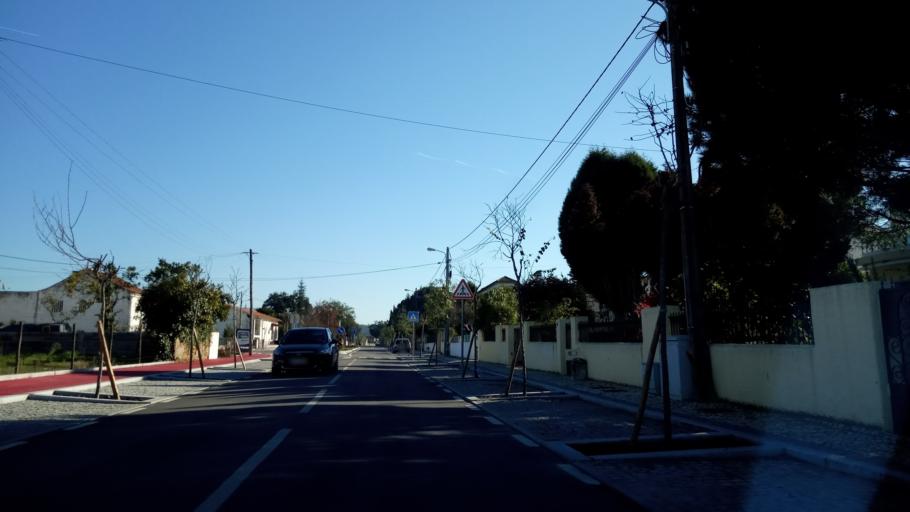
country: PT
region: Aveiro
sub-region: Anadia
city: Anadia
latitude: 40.4342
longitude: -8.4325
